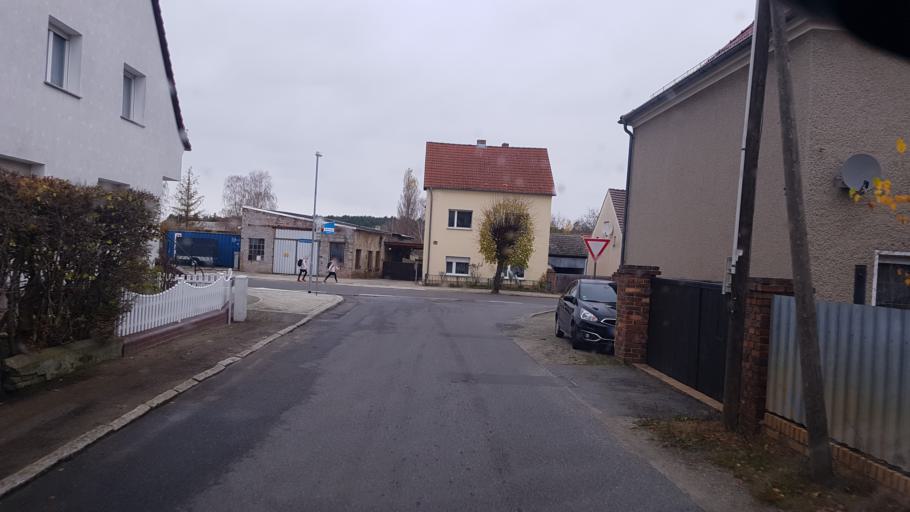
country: DE
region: Brandenburg
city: Crinitz
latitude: 51.7394
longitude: 13.7685
